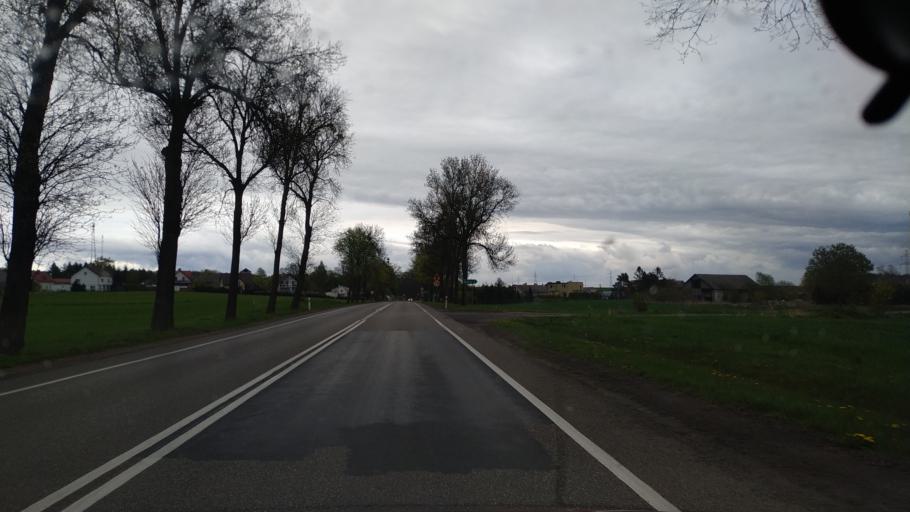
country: PL
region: Pomeranian Voivodeship
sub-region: Powiat starogardzki
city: Lubichowo
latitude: 53.9359
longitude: 18.4298
